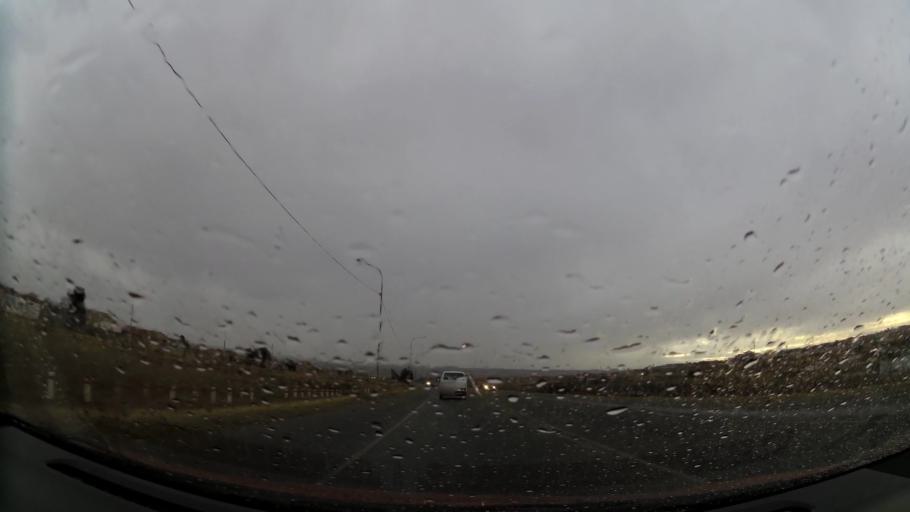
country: ZA
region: Gauteng
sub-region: City of Johannesburg Metropolitan Municipality
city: Roodepoort
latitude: -26.1715
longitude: 27.7897
